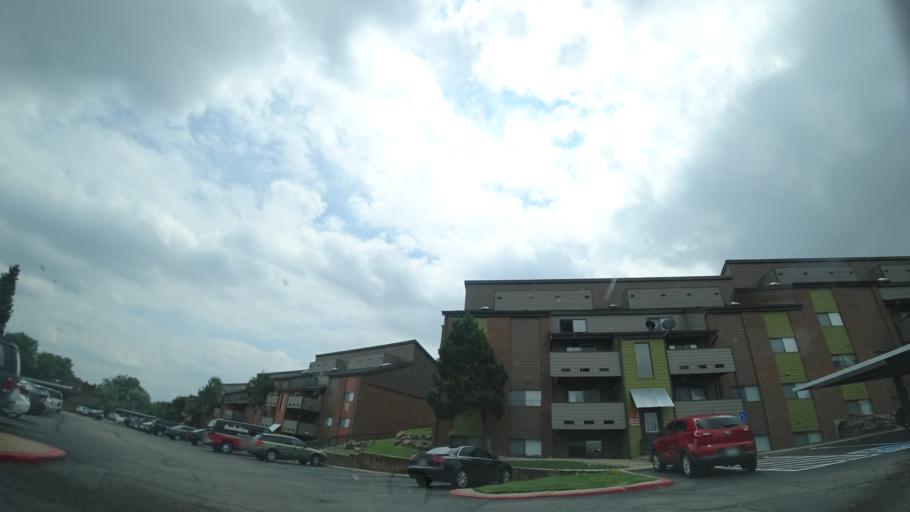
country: US
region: Colorado
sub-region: Jefferson County
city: West Pleasant View
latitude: 39.7194
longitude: -105.1466
